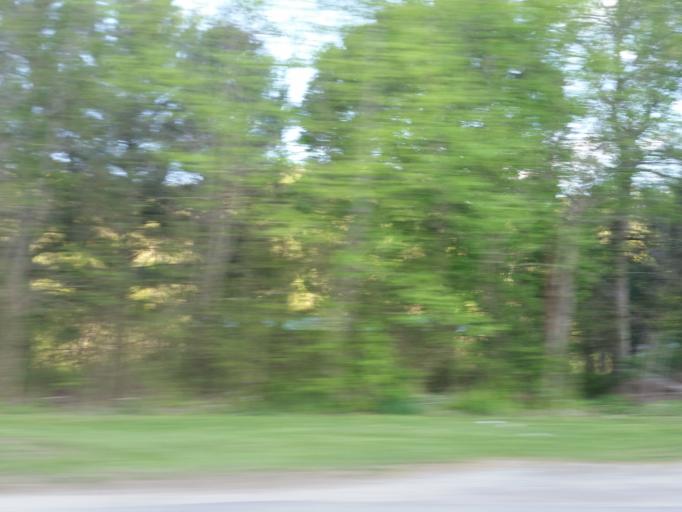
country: US
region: Tennessee
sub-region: Campbell County
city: Fincastle
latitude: 36.5671
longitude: -83.9307
